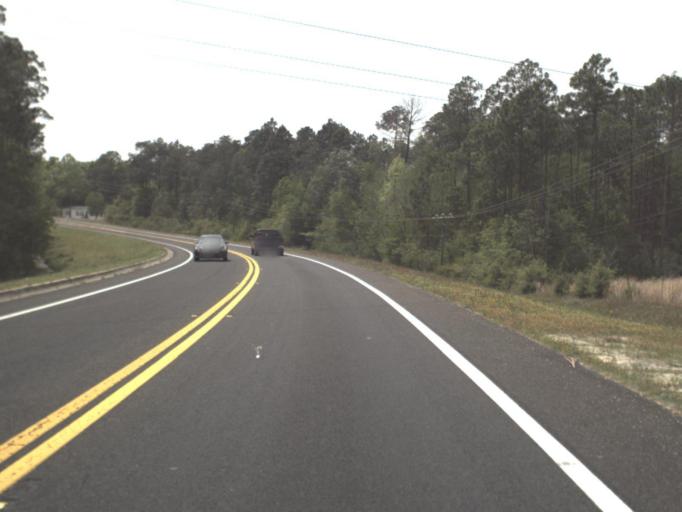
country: US
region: Florida
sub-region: Escambia County
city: Bellview
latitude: 30.4868
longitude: -87.3205
